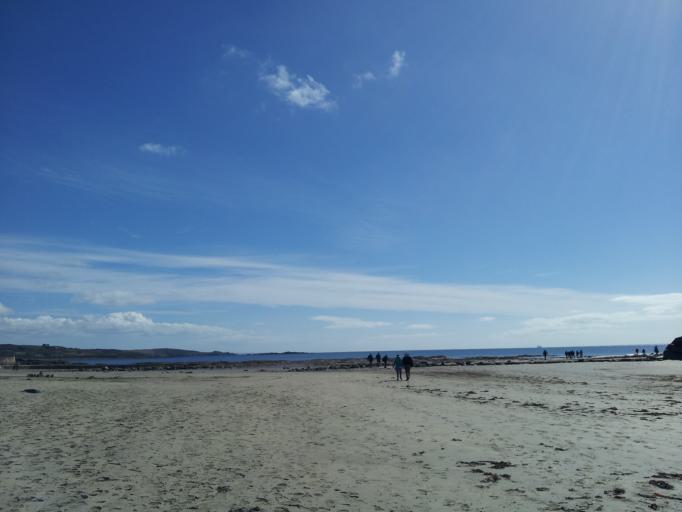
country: GB
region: England
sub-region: Cornwall
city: Marazion
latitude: 50.1234
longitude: -5.4756
